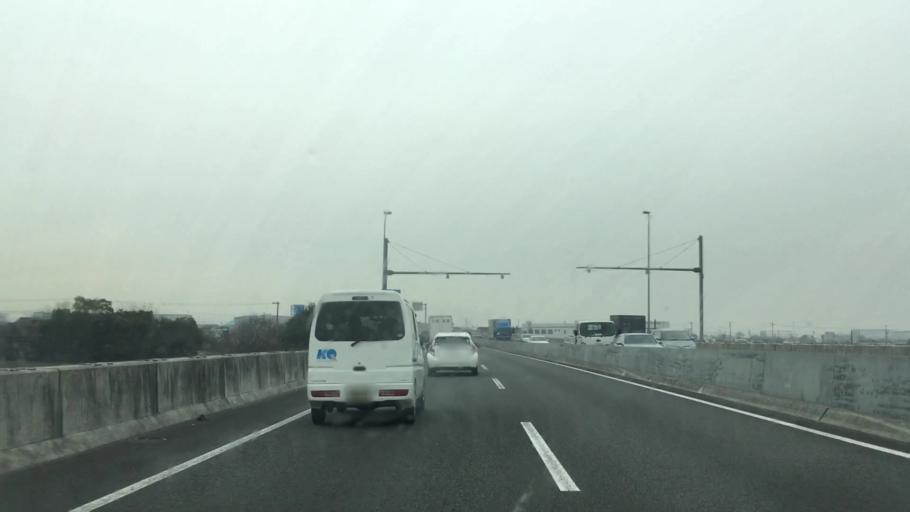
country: JP
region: Aichi
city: Anjo
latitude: 34.9357
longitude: 137.0426
